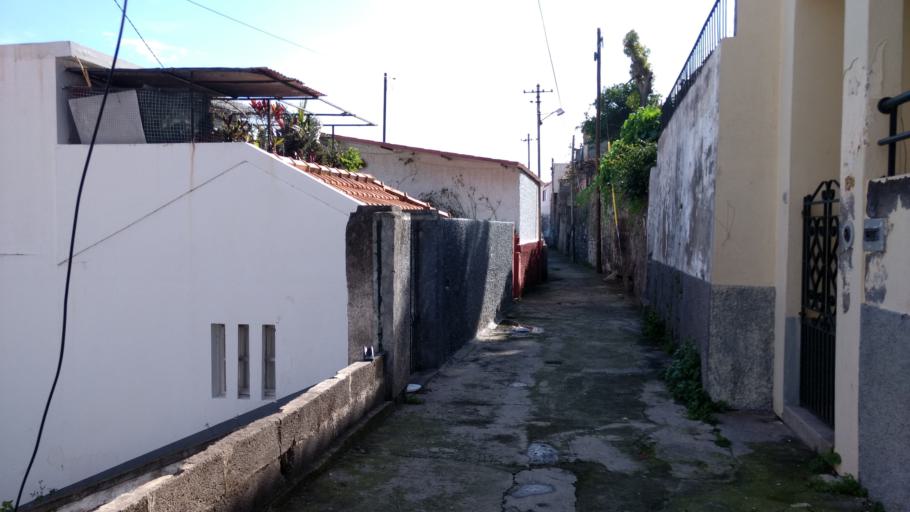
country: PT
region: Madeira
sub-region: Funchal
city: Nossa Senhora do Monte
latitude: 32.6546
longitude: -16.9154
